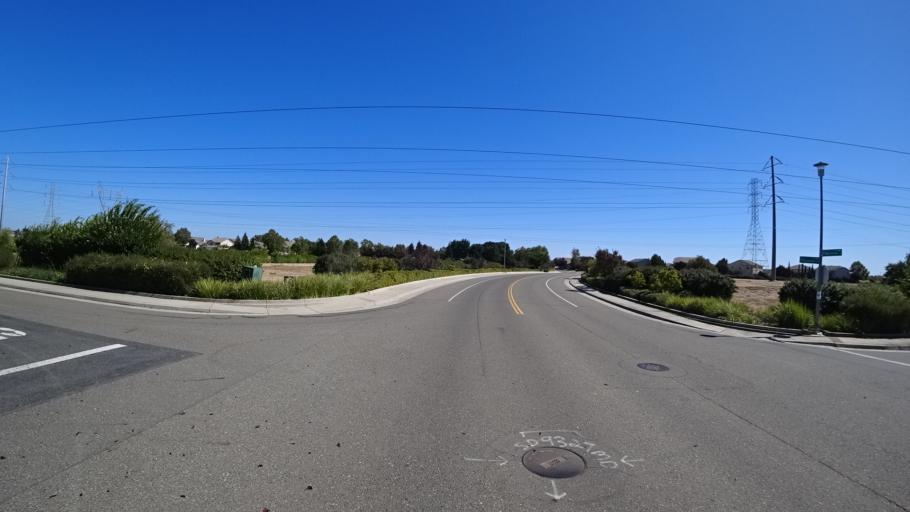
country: US
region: California
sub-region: Sacramento County
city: Elk Grove
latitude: 38.4026
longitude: -121.3512
